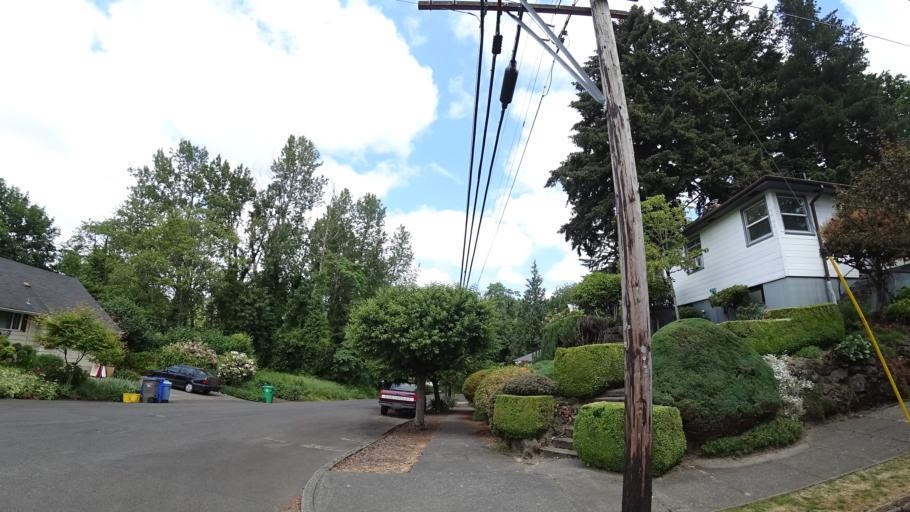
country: US
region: Oregon
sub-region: Clackamas County
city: Lake Oswego
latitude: 45.4682
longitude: -122.6898
